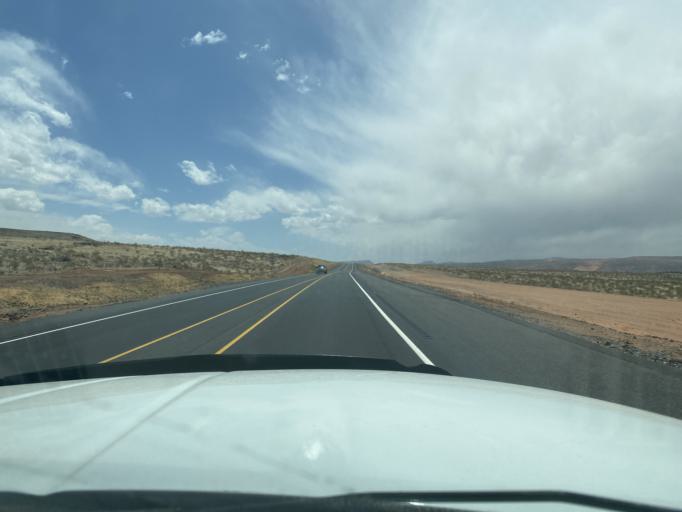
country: US
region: Utah
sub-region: Washington County
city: Hurricane
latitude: 37.1635
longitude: -113.3459
